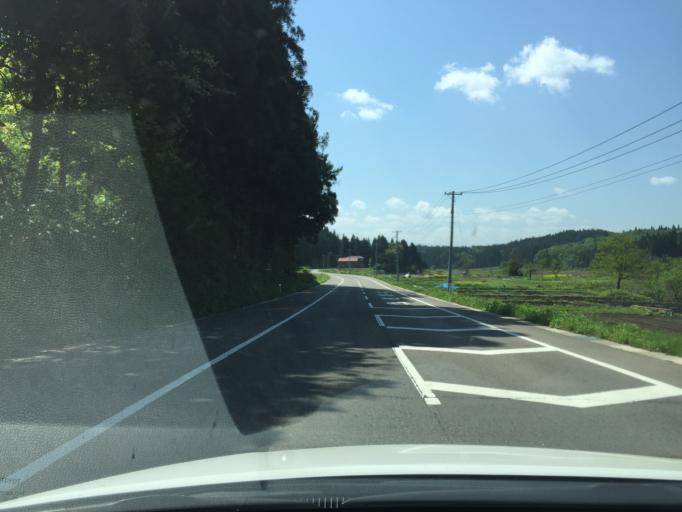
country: JP
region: Niigata
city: Kamo
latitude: 37.5707
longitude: 139.0837
